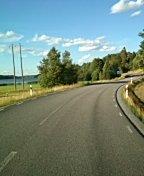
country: SE
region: Uppsala
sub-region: Habo Kommun
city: Balsta
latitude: 59.6268
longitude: 17.4969
